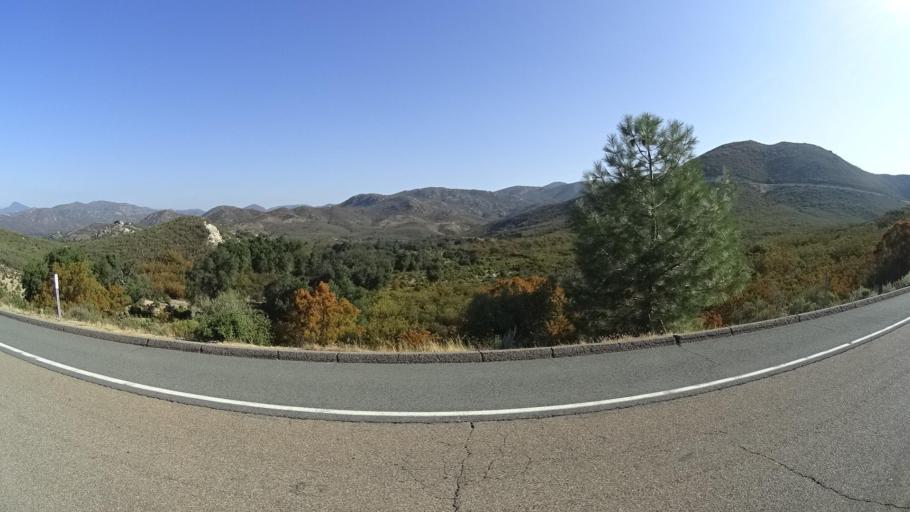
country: US
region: California
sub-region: San Diego County
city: Pine Valley
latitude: 32.8160
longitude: -116.5162
